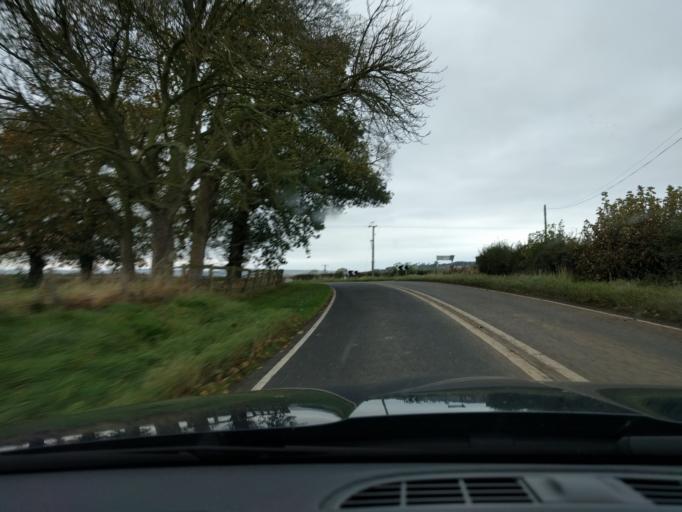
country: GB
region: England
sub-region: Northumberland
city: Ford
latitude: 55.7298
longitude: -2.0929
